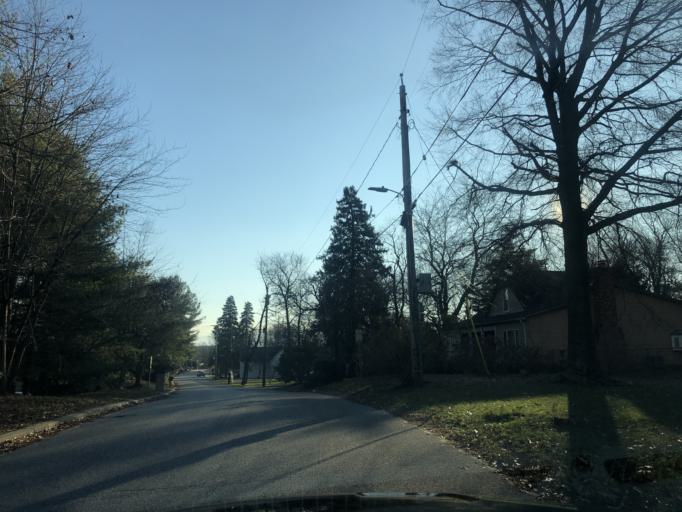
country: US
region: Maryland
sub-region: Anne Arundel County
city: Odenton
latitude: 39.0876
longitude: -76.7105
